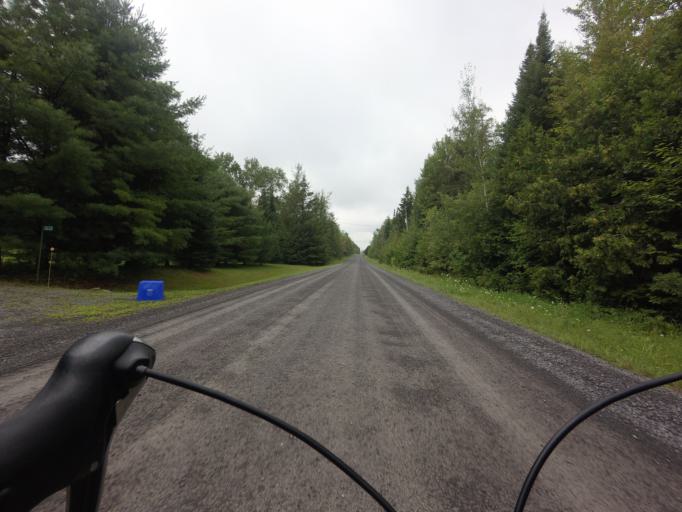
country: CA
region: Ontario
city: Bells Corners
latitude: 45.0305
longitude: -75.7568
